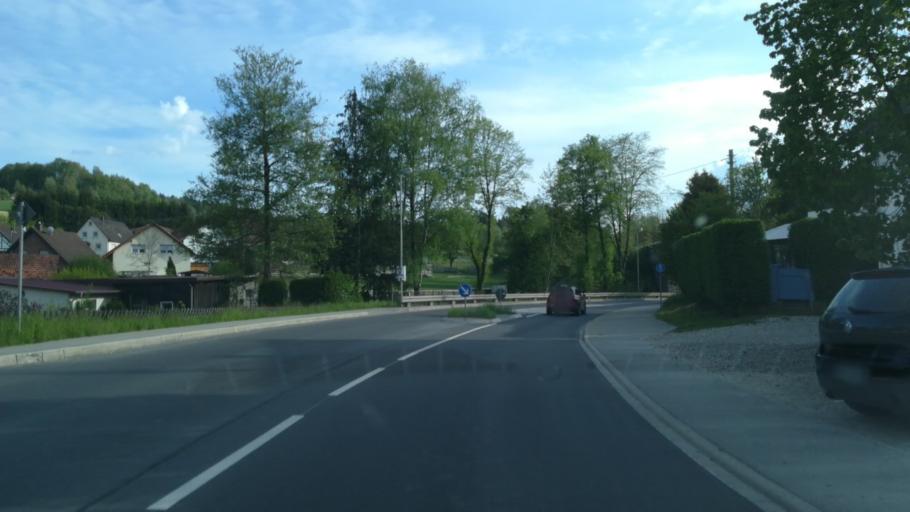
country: DE
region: Baden-Wuerttemberg
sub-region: Freiburg Region
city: Muhlingen
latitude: 47.8916
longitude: 9.0081
